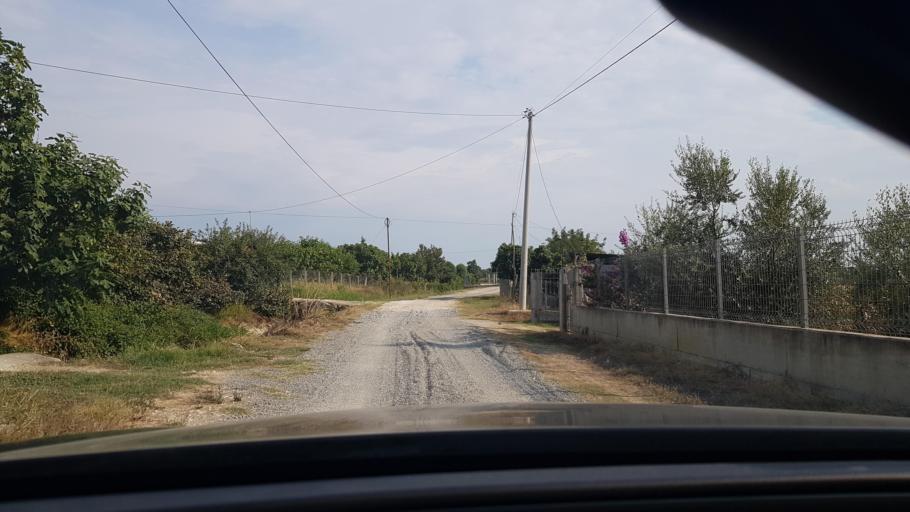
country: AL
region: Durres
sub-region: Rrethi i Durresit
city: Manze
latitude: 41.4729
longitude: 19.5667
